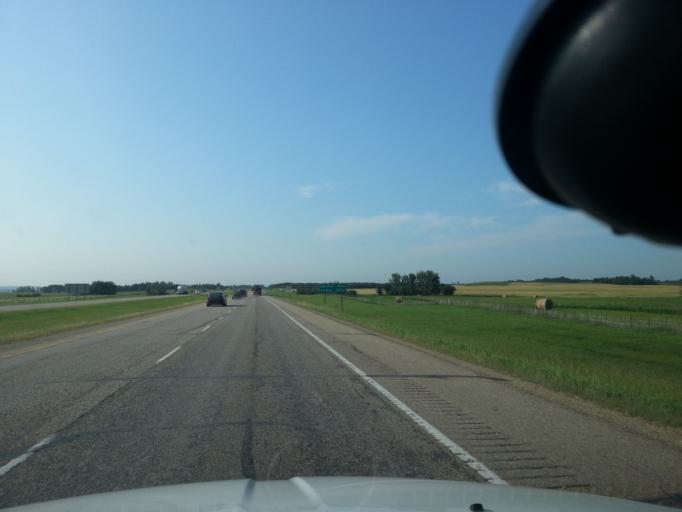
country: CA
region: Alberta
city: Millet
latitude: 52.9544
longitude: -113.6462
